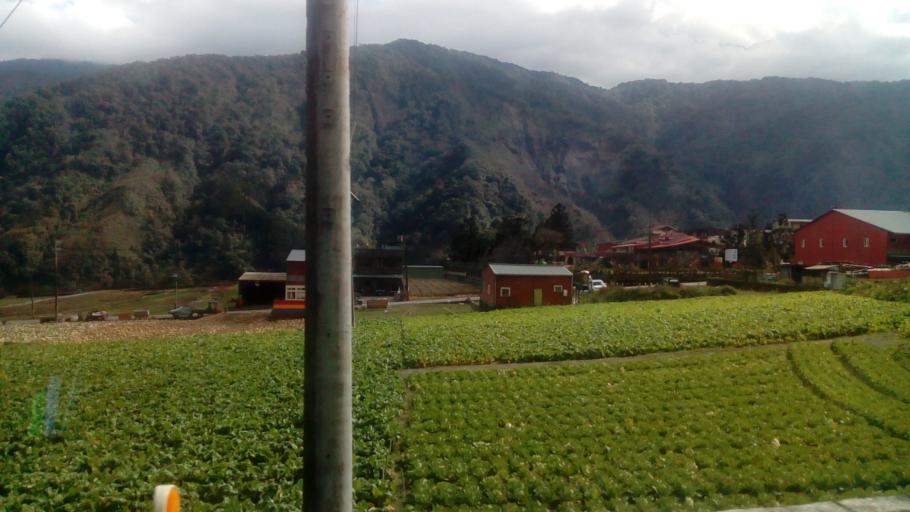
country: TW
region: Taiwan
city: Daxi
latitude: 24.4389
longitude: 121.3792
